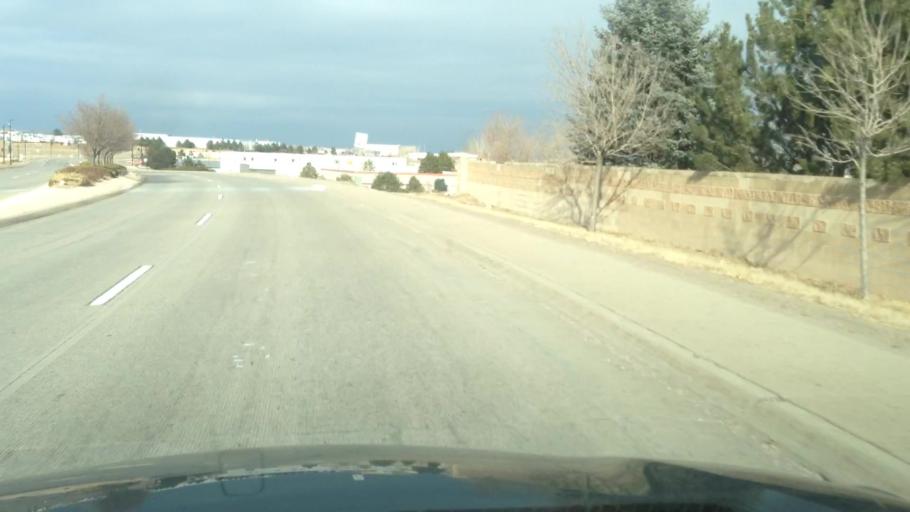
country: US
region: Colorado
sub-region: Arapahoe County
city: Dove Valley
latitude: 39.5802
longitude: -104.8090
